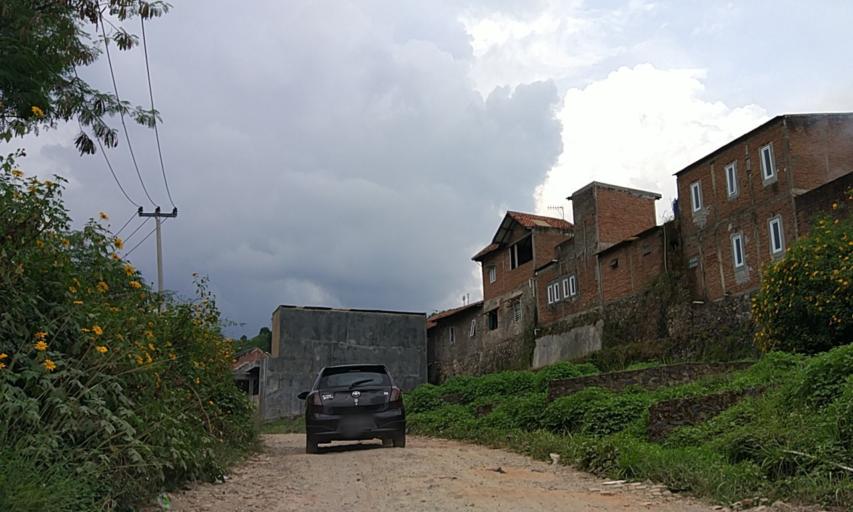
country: ID
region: West Java
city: Cileunyi
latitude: -6.9000
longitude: 107.6942
